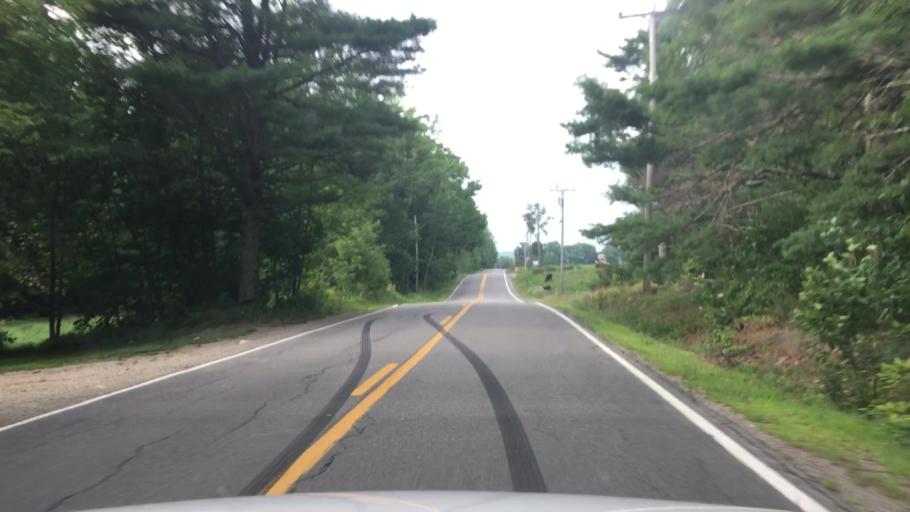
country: US
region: Maine
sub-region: Knox County
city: Washington
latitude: 44.2994
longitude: -69.3618
